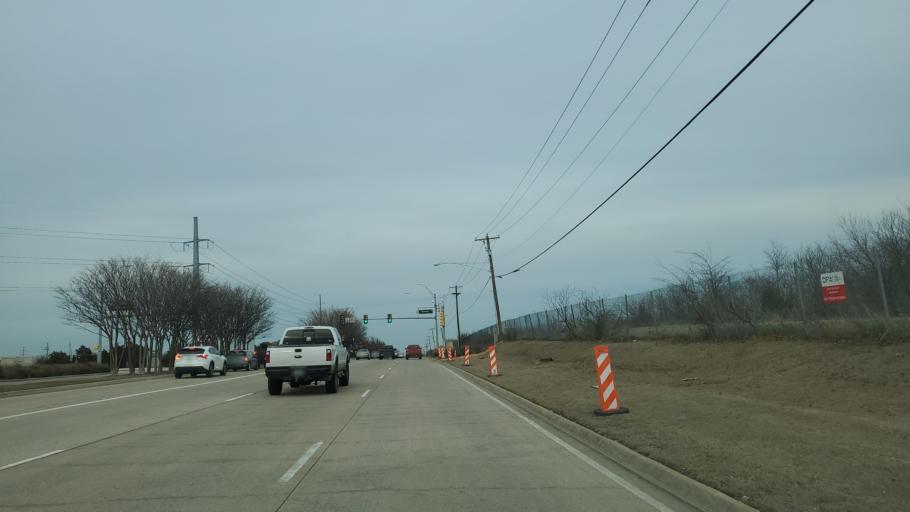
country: US
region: Texas
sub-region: Tarrant County
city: Grapevine
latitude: 32.9483
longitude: -97.0557
